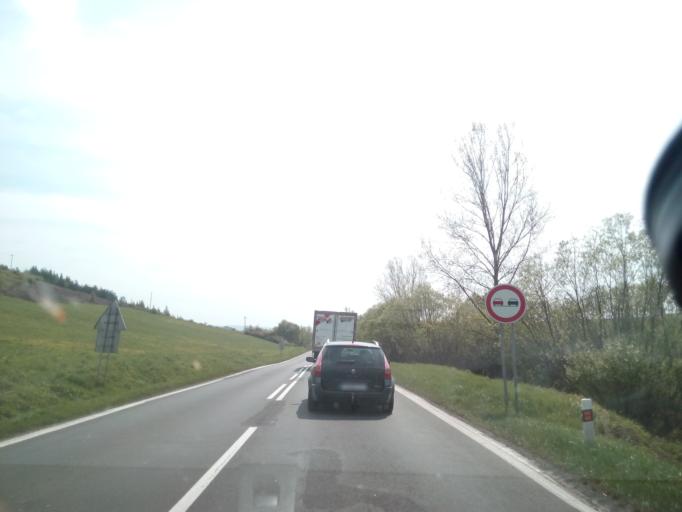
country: SK
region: Presovsky
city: Giraltovce
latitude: 49.0407
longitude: 21.4484
